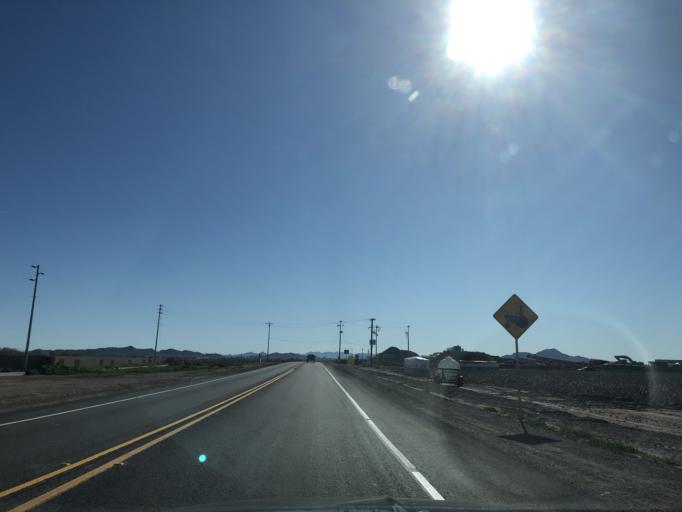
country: US
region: Arizona
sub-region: Maricopa County
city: Buckeye
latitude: 33.3755
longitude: -112.4778
